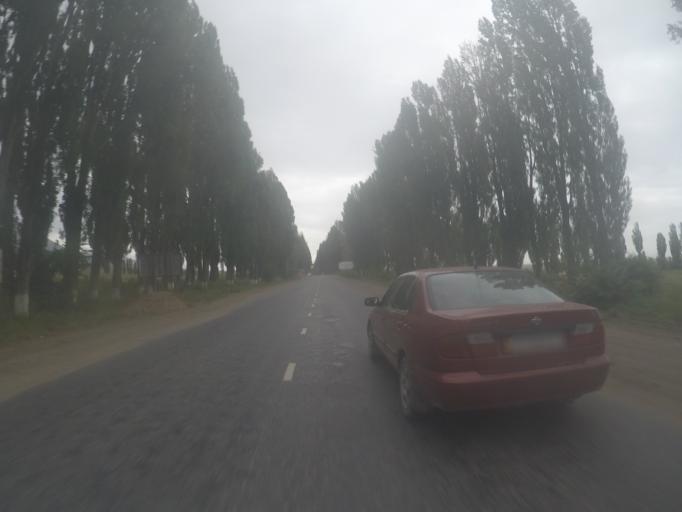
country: KG
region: Ysyk-Koel
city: Cholpon-Ata
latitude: 42.6924
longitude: 77.3767
